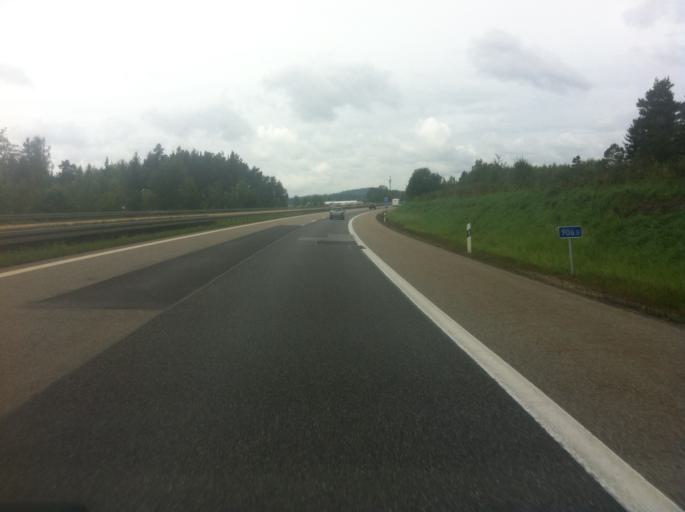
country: DE
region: Bavaria
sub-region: Upper Palatinate
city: Waidhaus
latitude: 49.6314
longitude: 12.5003
